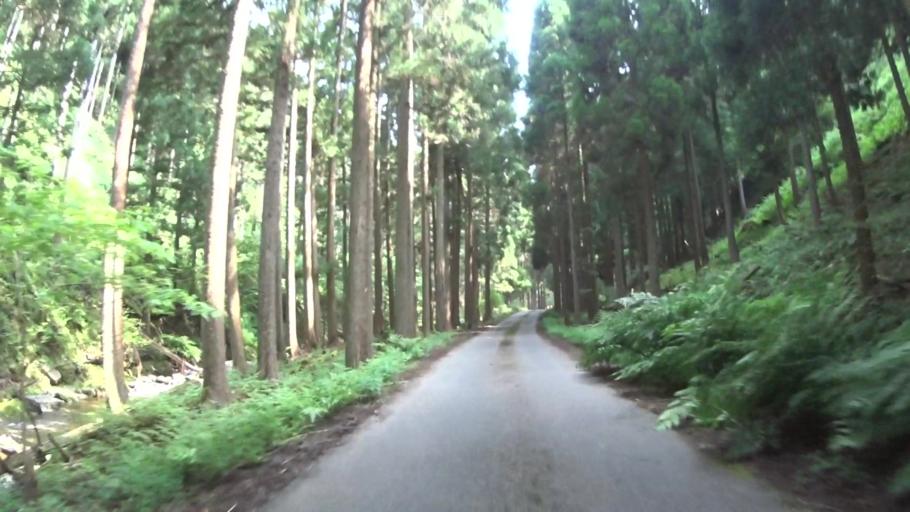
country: JP
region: Fukui
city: Obama
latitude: 35.2798
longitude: 135.6408
